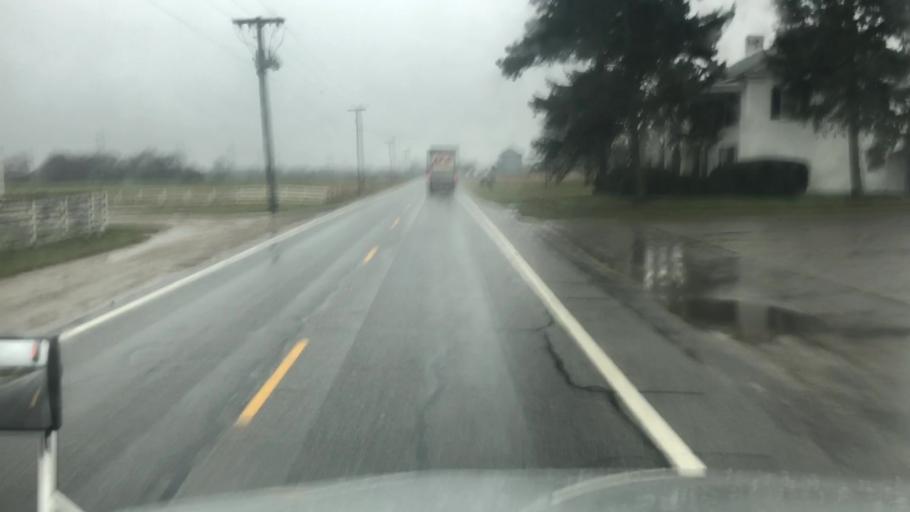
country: US
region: Ohio
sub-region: Union County
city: New California
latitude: 40.2015
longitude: -83.1921
